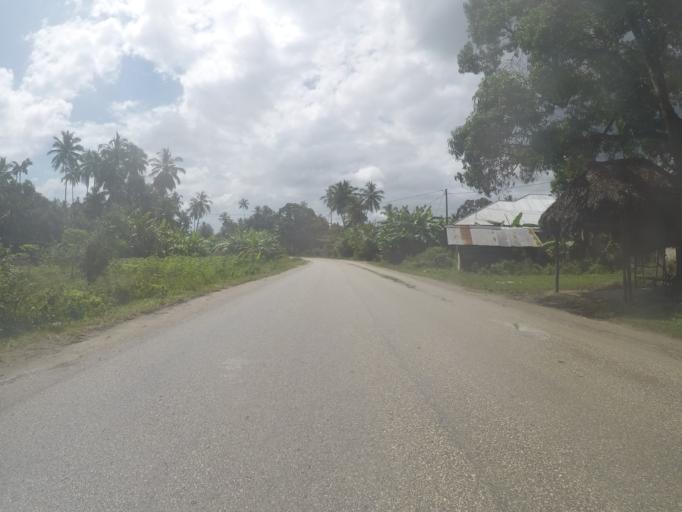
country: TZ
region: Zanzibar North
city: Gamba
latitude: -5.9831
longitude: 39.2509
